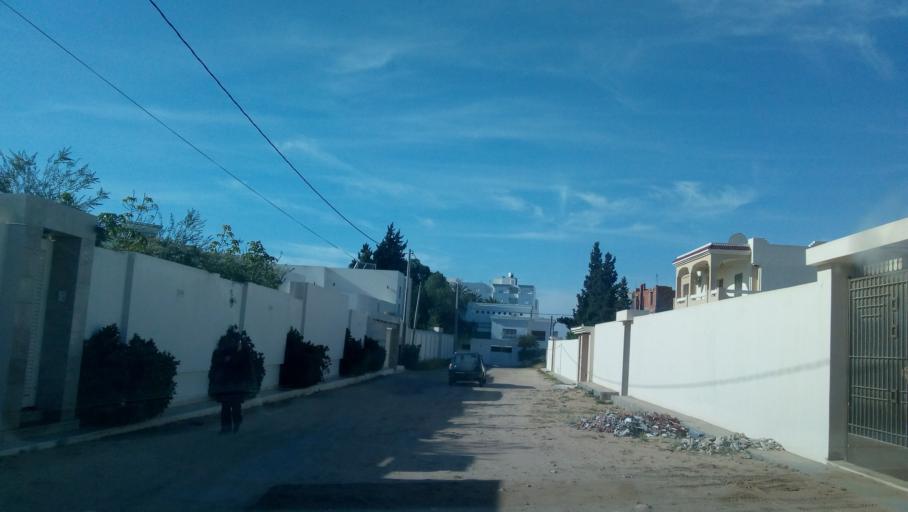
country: TN
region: Safaqis
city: Sfax
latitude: 34.7525
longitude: 10.7332
